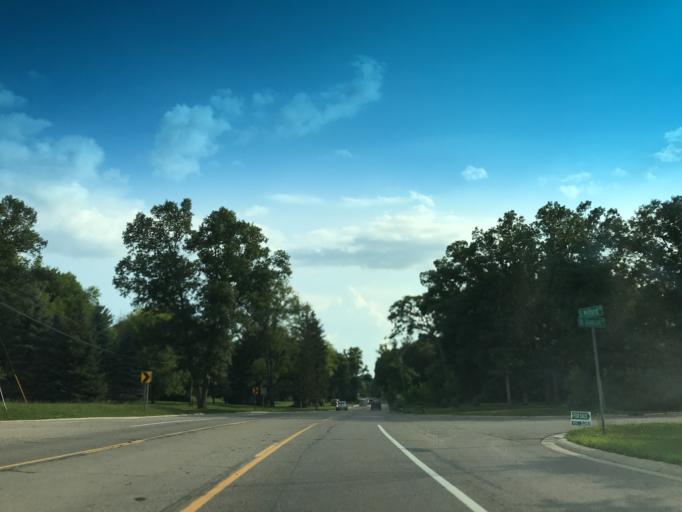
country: US
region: Michigan
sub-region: Oakland County
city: Milford
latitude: 42.5656
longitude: -83.6168
